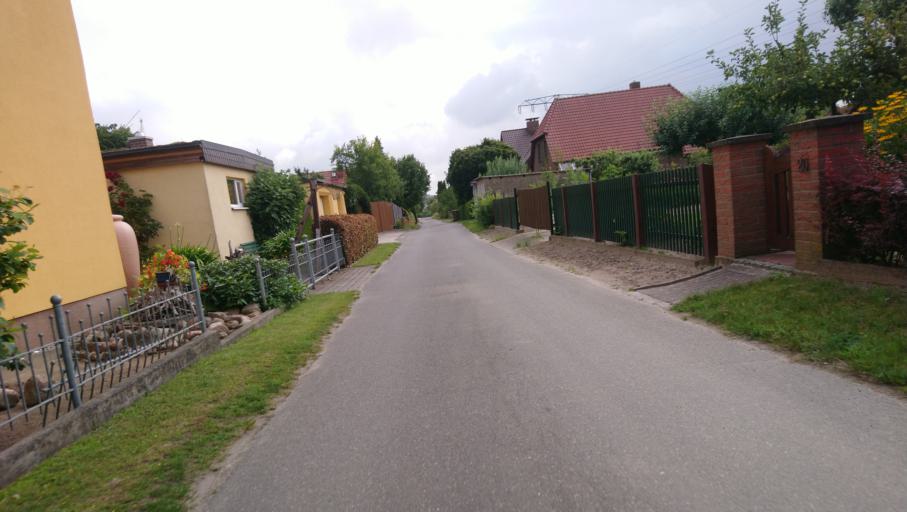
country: DE
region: Mecklenburg-Vorpommern
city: Papendorf
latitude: 54.0664
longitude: 12.1061
